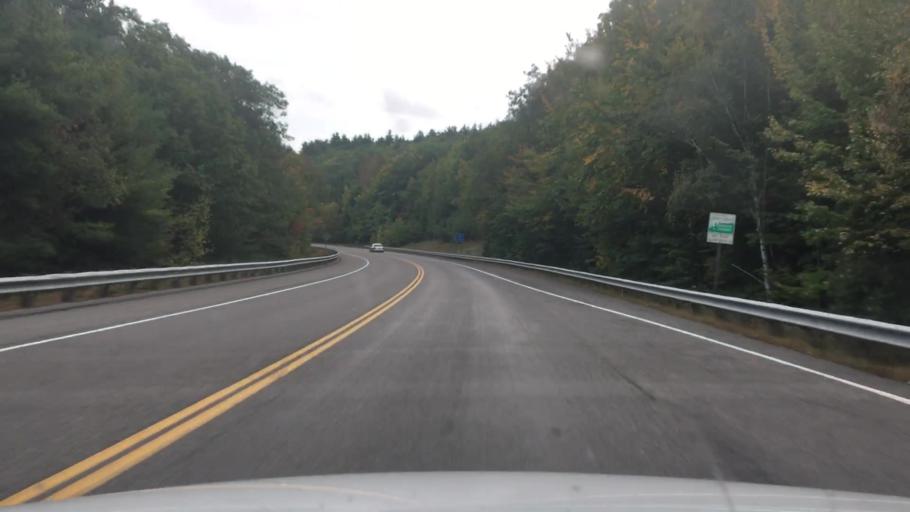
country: US
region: New Hampshire
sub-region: Carroll County
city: Wolfeboro
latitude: 43.5195
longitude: -71.2726
